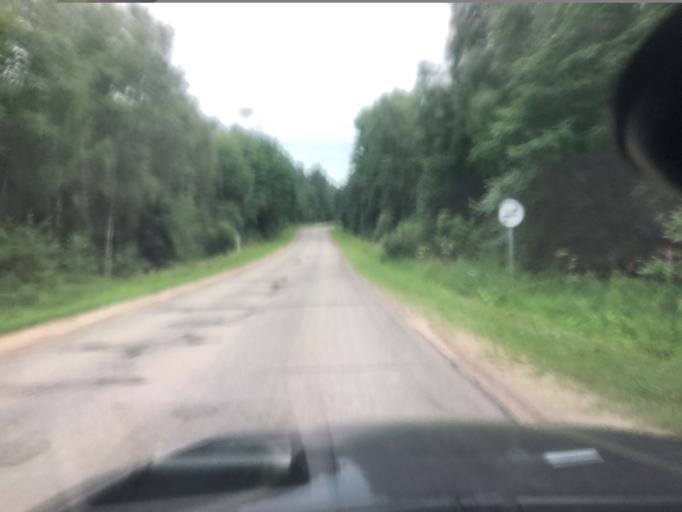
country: RU
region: Jaroslavl
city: Petrovsk
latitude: 56.9868
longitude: 39.1963
